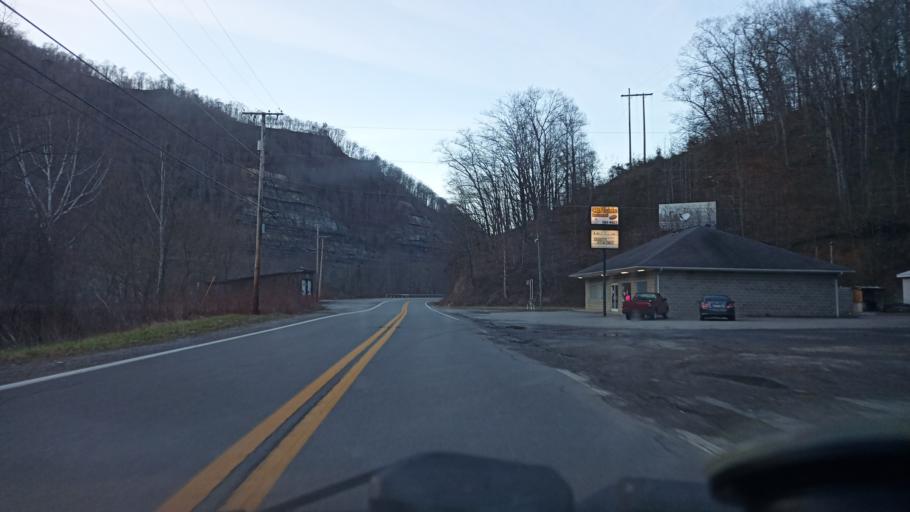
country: US
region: West Virginia
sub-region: Logan County
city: Mallory
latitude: 37.7492
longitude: -81.8904
